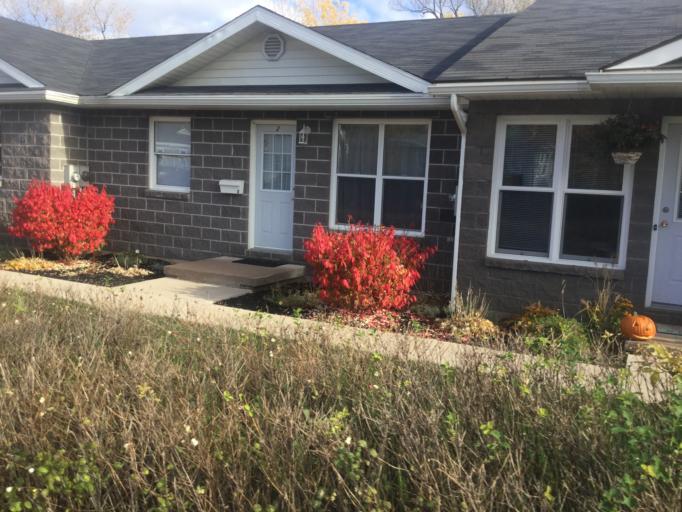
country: CA
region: Nova Scotia
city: New Glasgow
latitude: 45.5836
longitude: -62.6537
